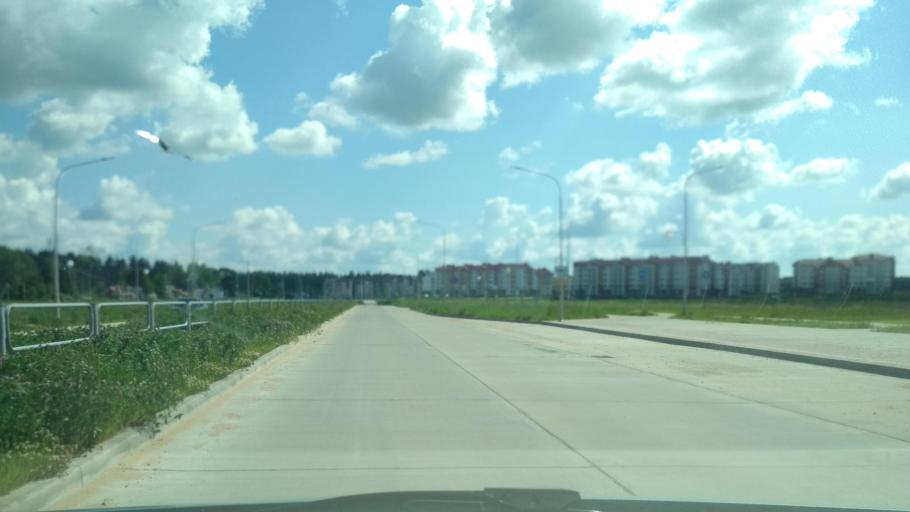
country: BY
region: Grodnenskaya
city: Astravyets
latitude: 54.5984
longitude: 25.9621
